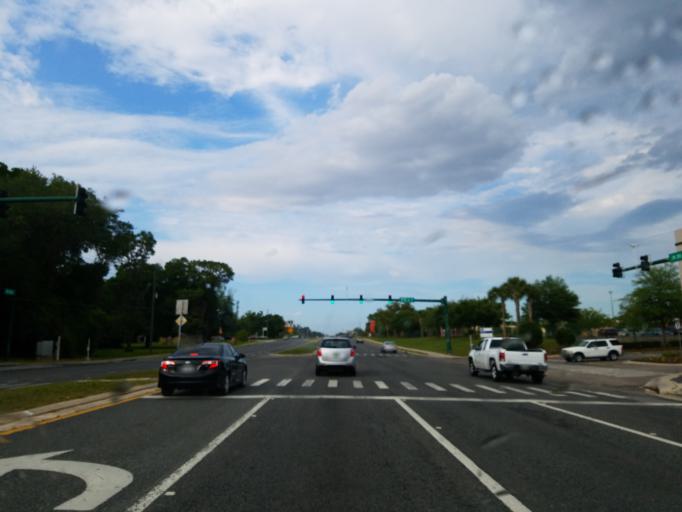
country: US
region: Florida
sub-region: Marion County
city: Ocala
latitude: 29.1402
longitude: -82.1952
